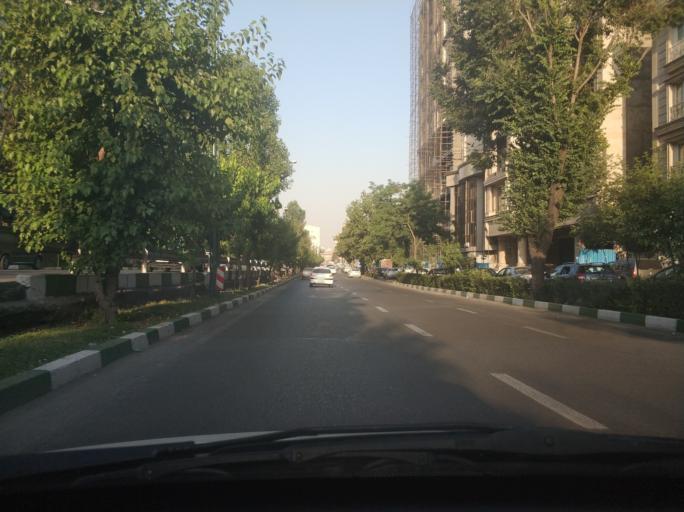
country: IR
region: Tehran
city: Tajrish
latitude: 35.7999
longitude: 51.4689
